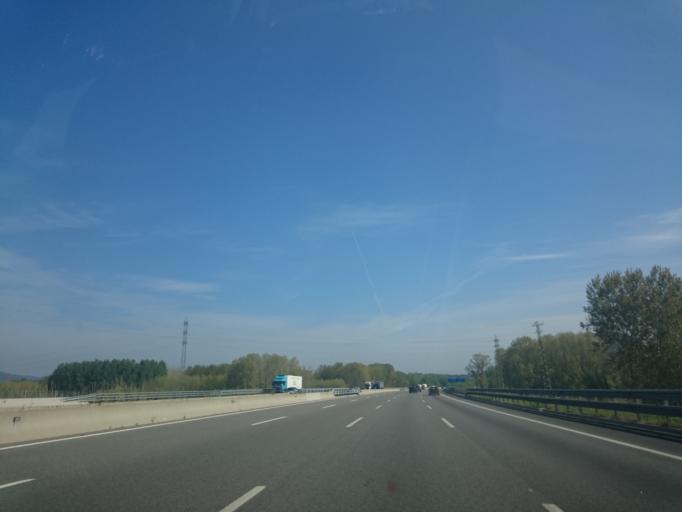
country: ES
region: Catalonia
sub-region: Provincia de Girona
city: Salt
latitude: 41.9761
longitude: 2.7789
